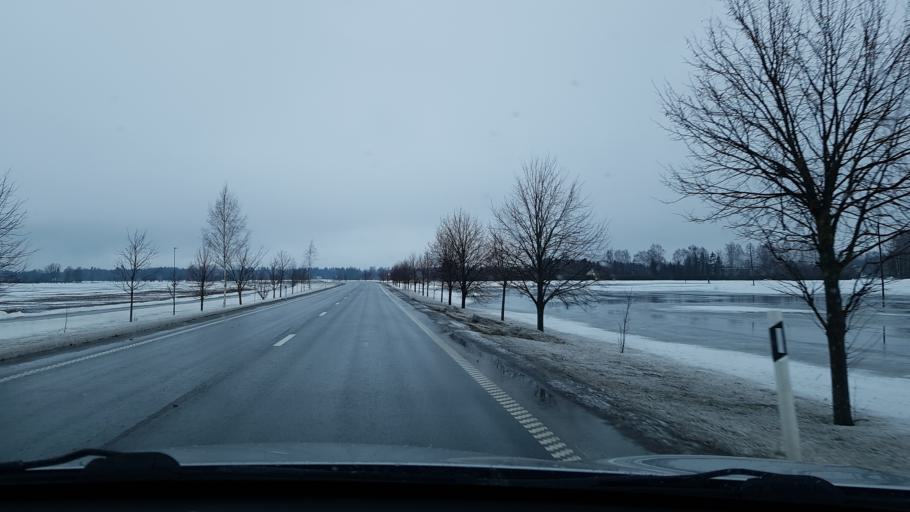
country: EE
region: Raplamaa
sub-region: Kehtna vald
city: Kehtna
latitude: 58.9329
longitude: 24.8803
